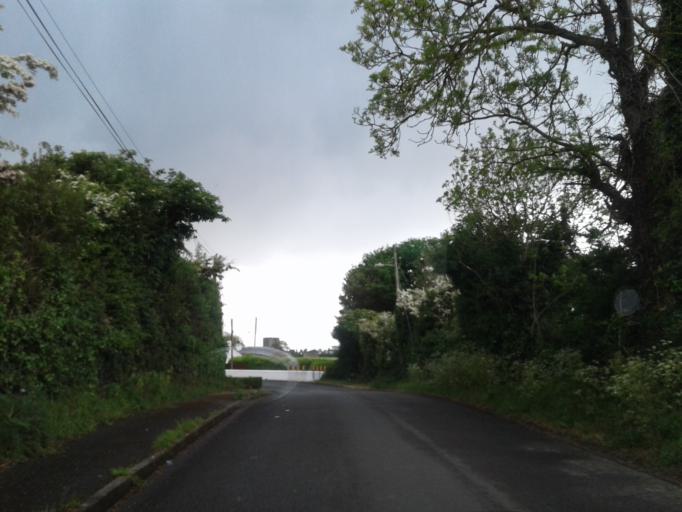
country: IE
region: Leinster
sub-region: Dublin City
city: Finglas
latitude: 53.4260
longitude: -6.3084
